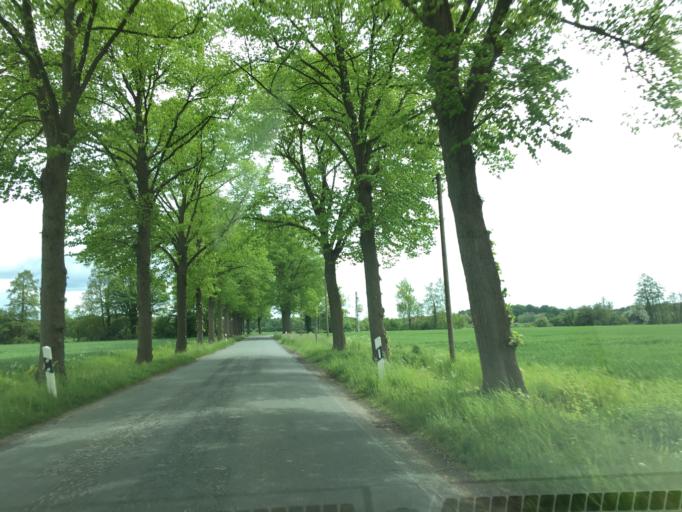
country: DE
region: North Rhine-Westphalia
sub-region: Regierungsbezirk Munster
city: Havixbeck
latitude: 51.9872
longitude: 7.4742
